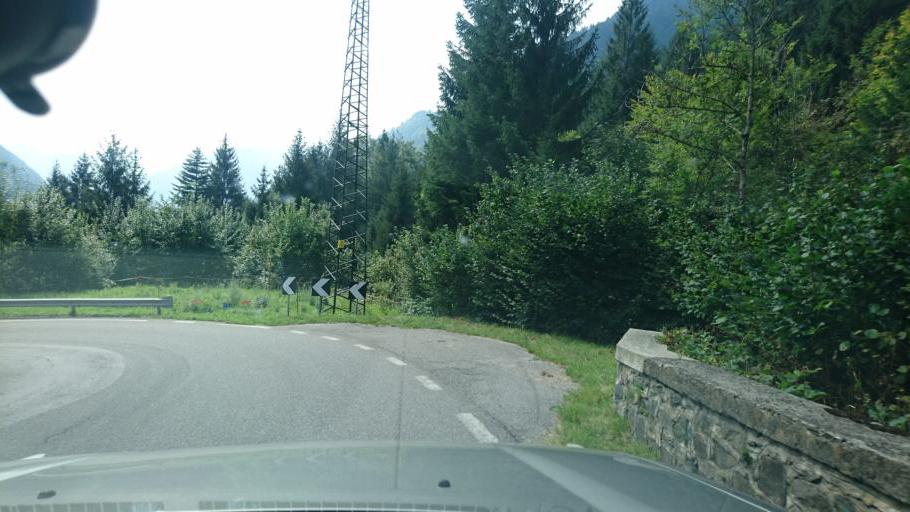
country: IT
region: Lombardy
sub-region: Provincia di Brescia
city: Bagolino
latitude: 45.8664
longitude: 10.4540
